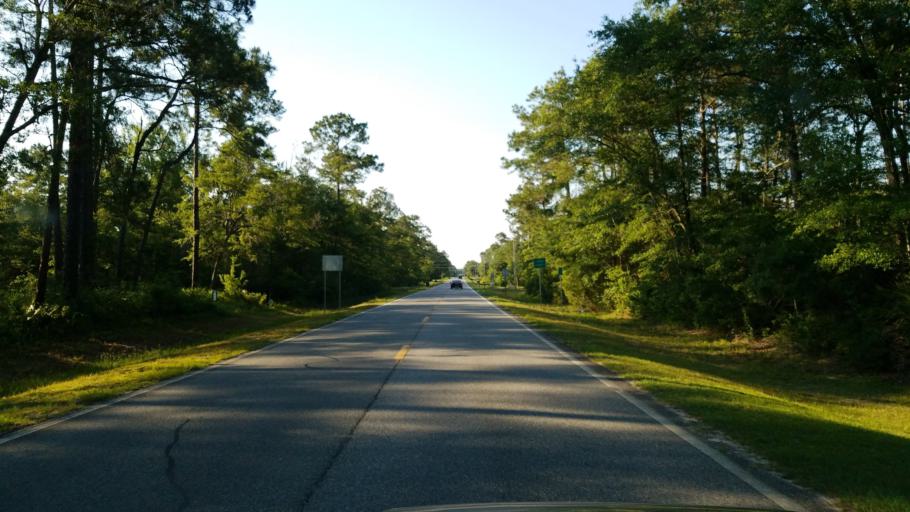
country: US
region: Georgia
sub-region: Lanier County
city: Lakeland
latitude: 30.9472
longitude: -83.0817
